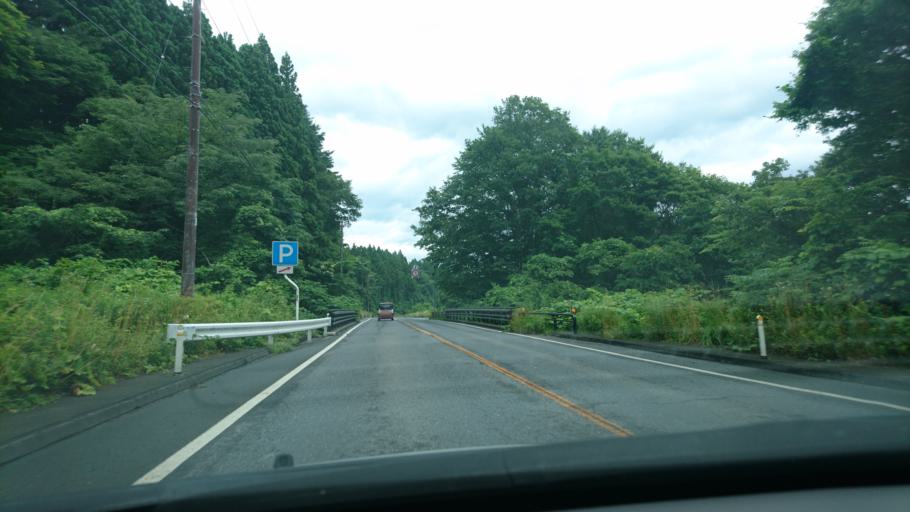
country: JP
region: Iwate
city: Yamada
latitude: 39.4114
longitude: 141.9619
